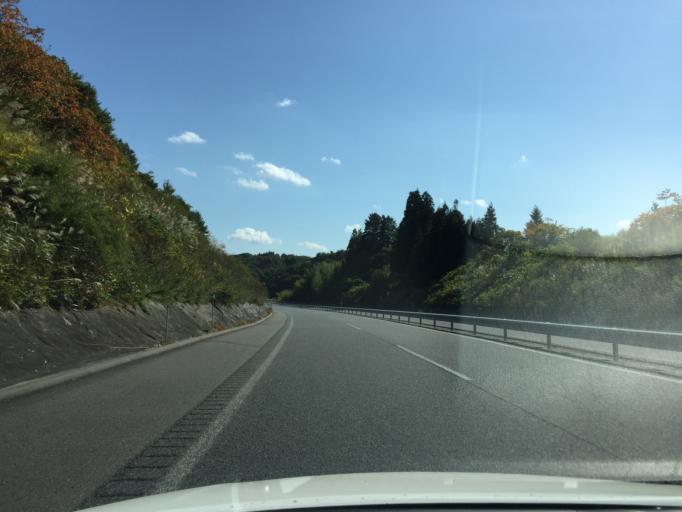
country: JP
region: Fukushima
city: Funehikimachi-funehiki
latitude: 37.2580
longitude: 140.6493
